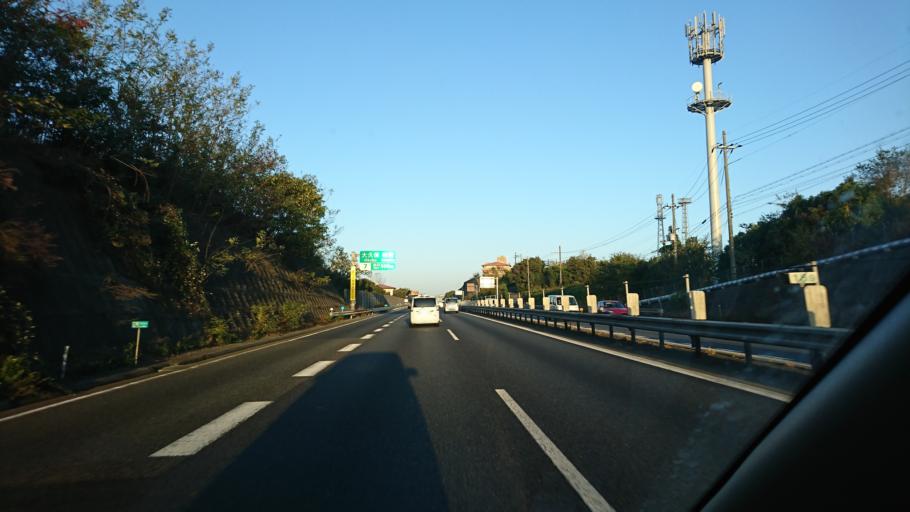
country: JP
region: Hyogo
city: Akashi
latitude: 34.7067
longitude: 134.9508
